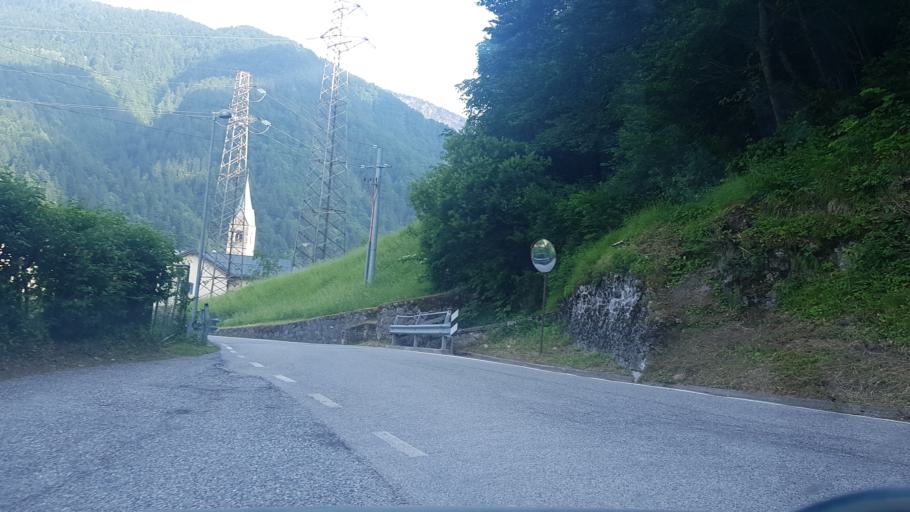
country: IT
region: Friuli Venezia Giulia
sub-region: Provincia di Udine
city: Pontebba
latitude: 46.5083
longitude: 13.3012
